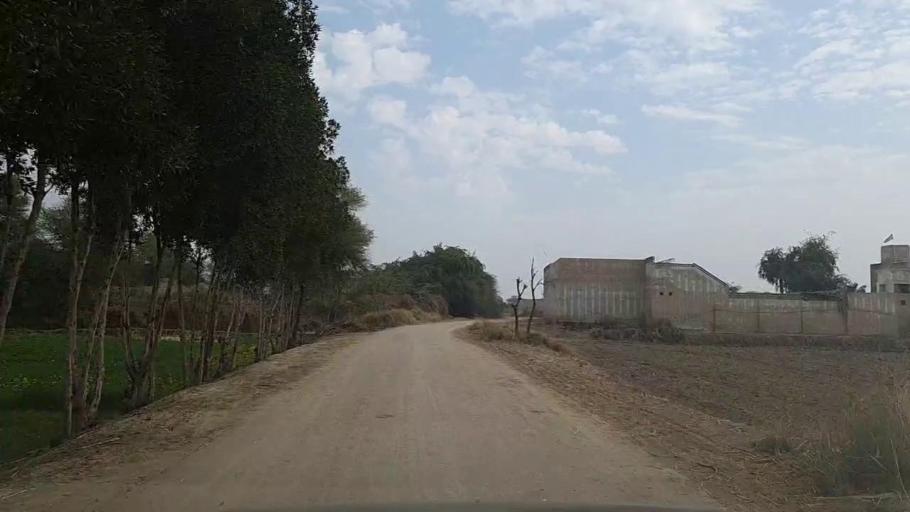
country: PK
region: Sindh
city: Daur
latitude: 26.3914
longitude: 68.3589
